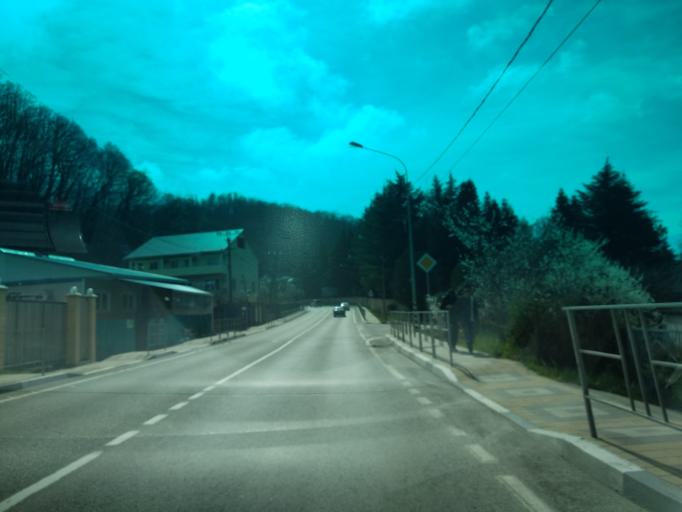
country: RU
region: Krasnodarskiy
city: Shepsi
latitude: 44.0385
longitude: 39.1505
